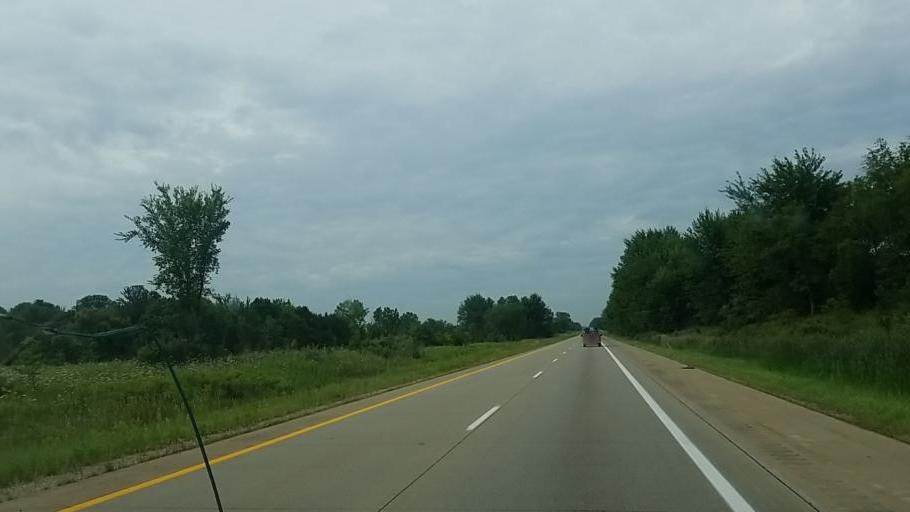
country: US
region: Michigan
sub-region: Branch County
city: Coldwater
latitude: 42.0098
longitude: -84.9726
